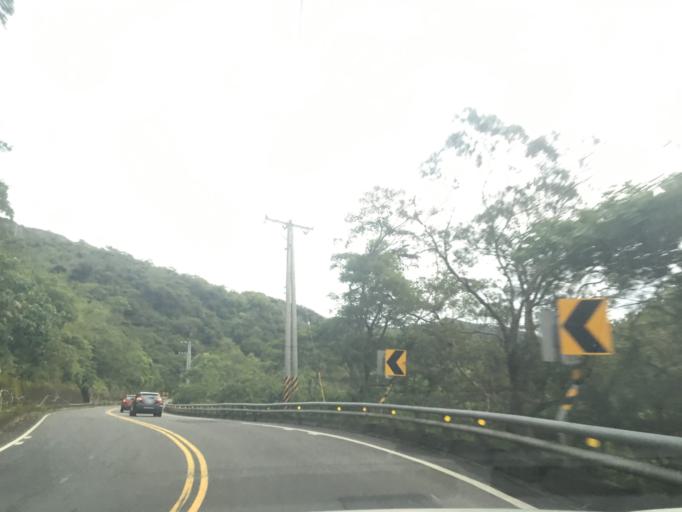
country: TW
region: Taiwan
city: Hengchun
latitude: 22.2230
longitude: 120.7964
